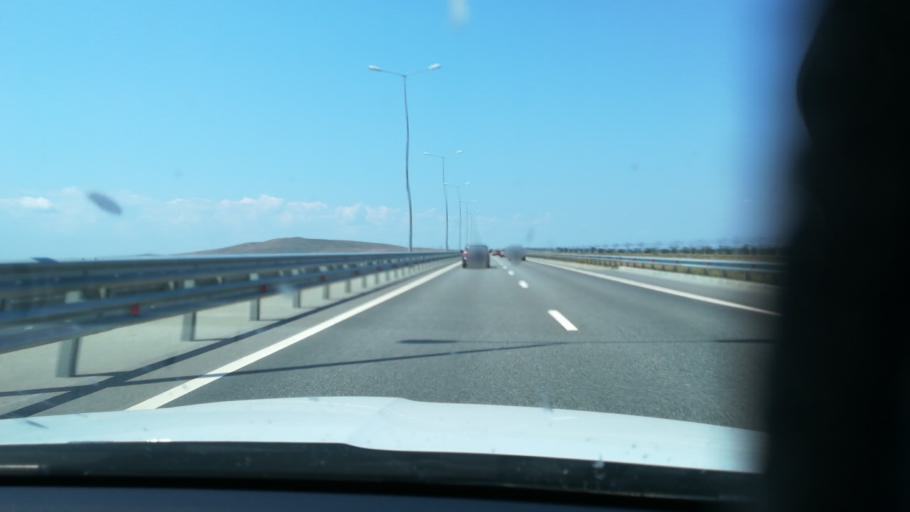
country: RU
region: Krasnodarskiy
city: Vyshestebliyevskaya
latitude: 45.2296
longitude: 36.9258
